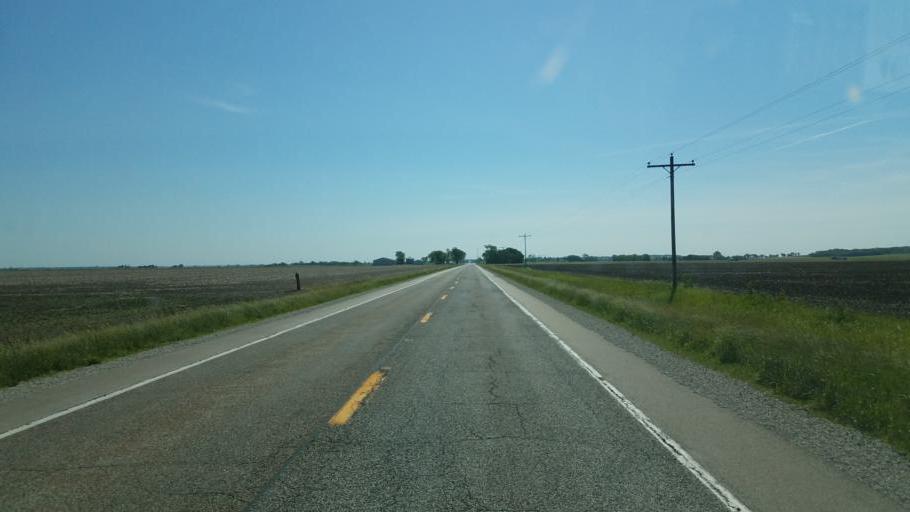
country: US
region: Illinois
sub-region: Mason County
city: Mason City
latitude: 40.3047
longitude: -89.7073
